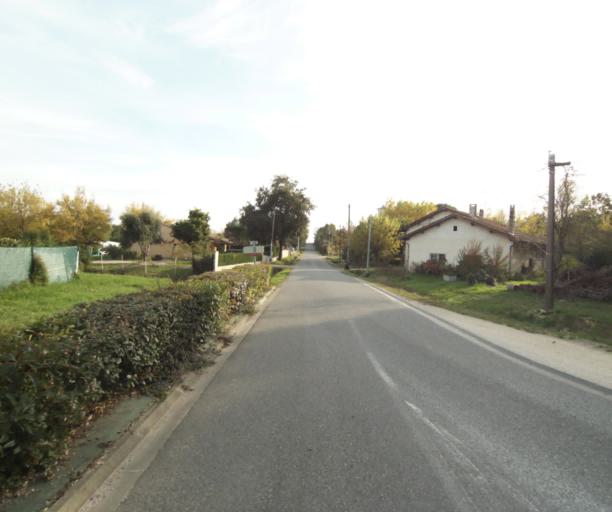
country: FR
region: Midi-Pyrenees
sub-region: Departement du Tarn-et-Garonne
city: Campsas
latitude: 43.8925
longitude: 1.3259
